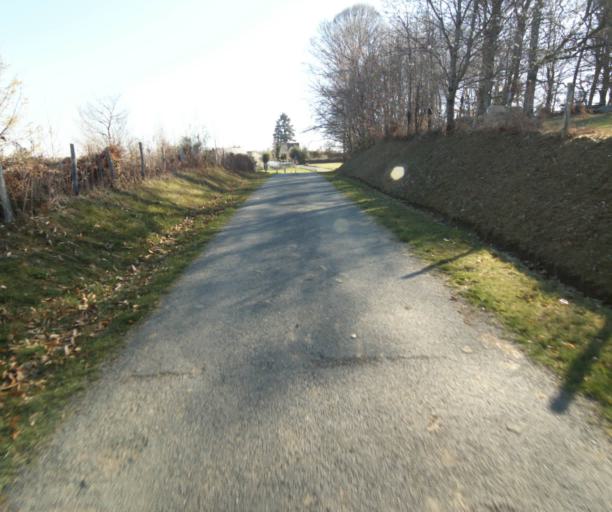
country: FR
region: Limousin
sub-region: Departement de la Correze
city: Saint-Clement
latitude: 45.3714
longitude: 1.6517
